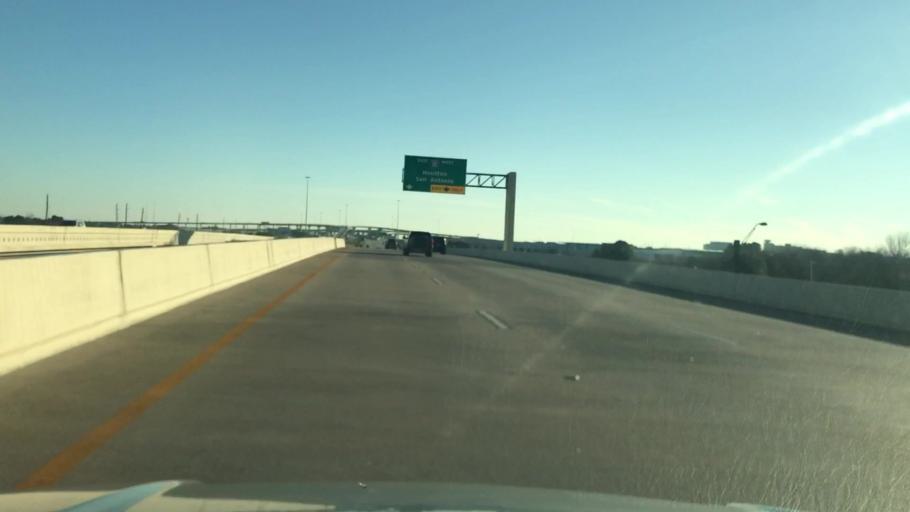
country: US
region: Texas
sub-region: Harris County
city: Katy
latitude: 29.8022
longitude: -95.7756
